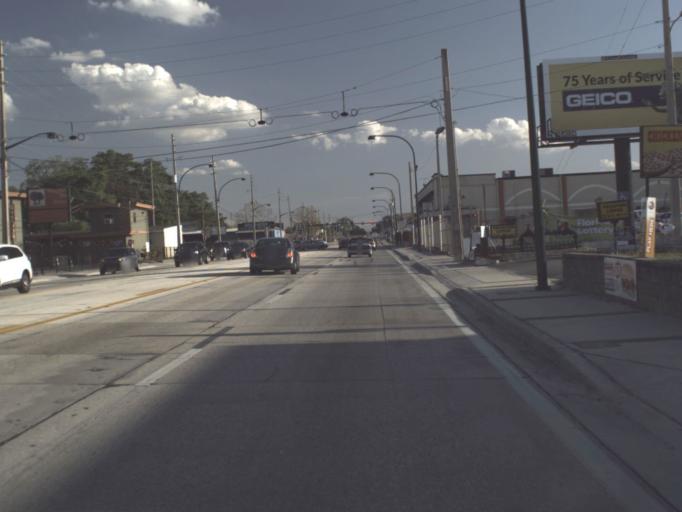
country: US
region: Florida
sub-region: Orange County
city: Orlando
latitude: 28.5342
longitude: -81.3973
